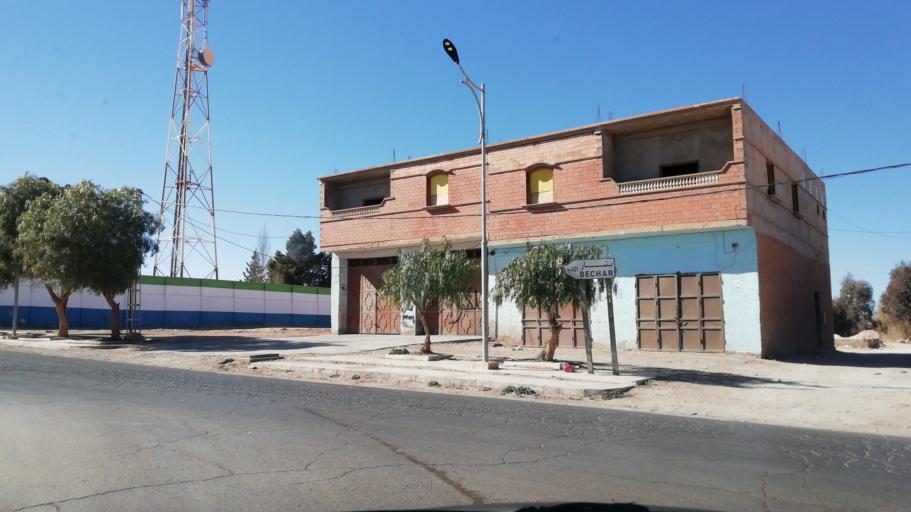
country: DZ
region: Saida
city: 'Ain el Hadjar
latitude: 34.0452
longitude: 0.0851
